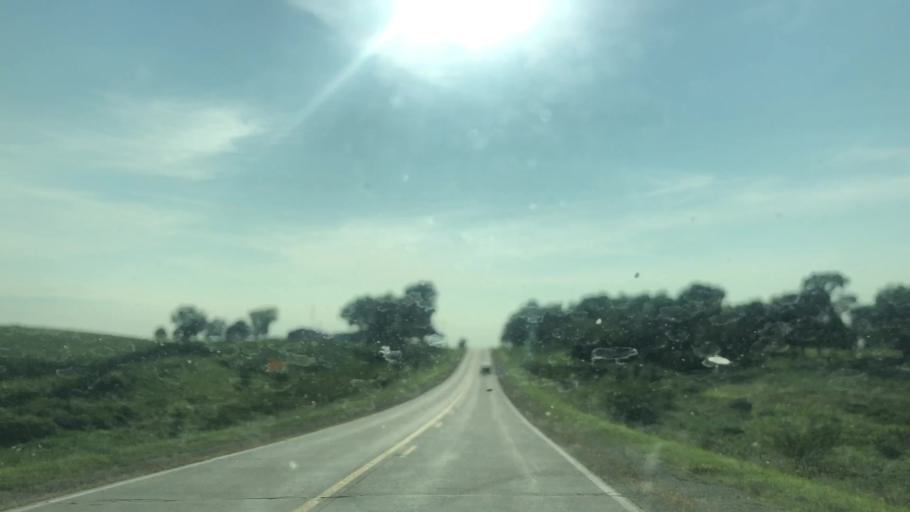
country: US
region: Iowa
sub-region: Marshall County
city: Marshalltown
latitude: 42.0489
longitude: -92.9871
